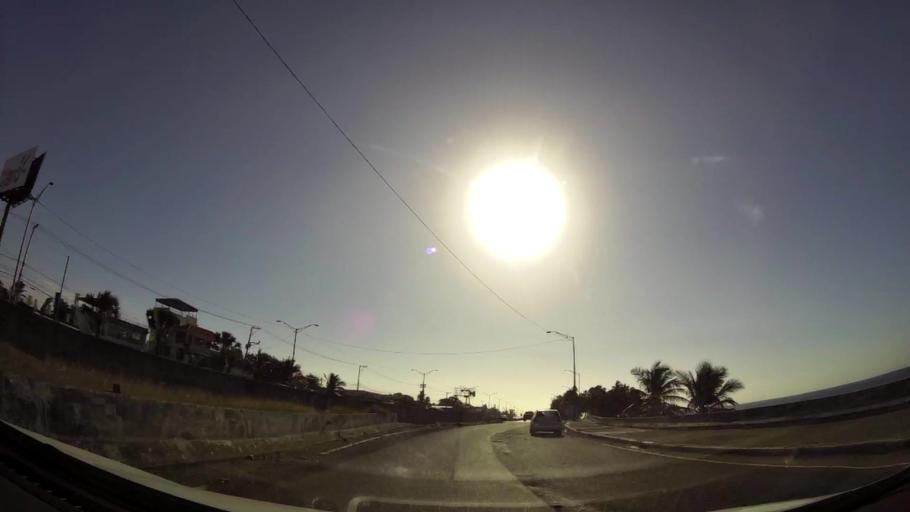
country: DO
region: Santo Domingo
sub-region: Santo Domingo
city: Santo Domingo Este
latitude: 18.4670
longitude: -69.8264
